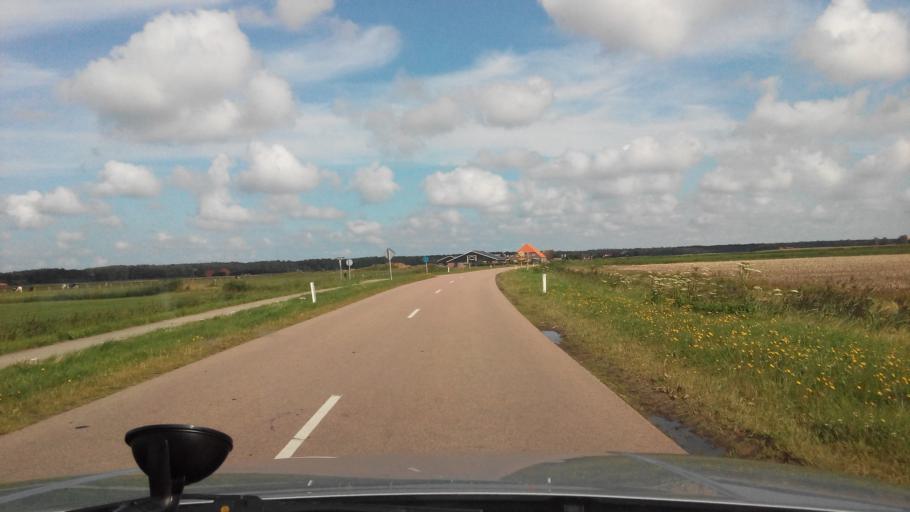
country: NL
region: North Holland
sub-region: Gemeente Texel
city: Den Burg
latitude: 53.0355
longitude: 4.7506
